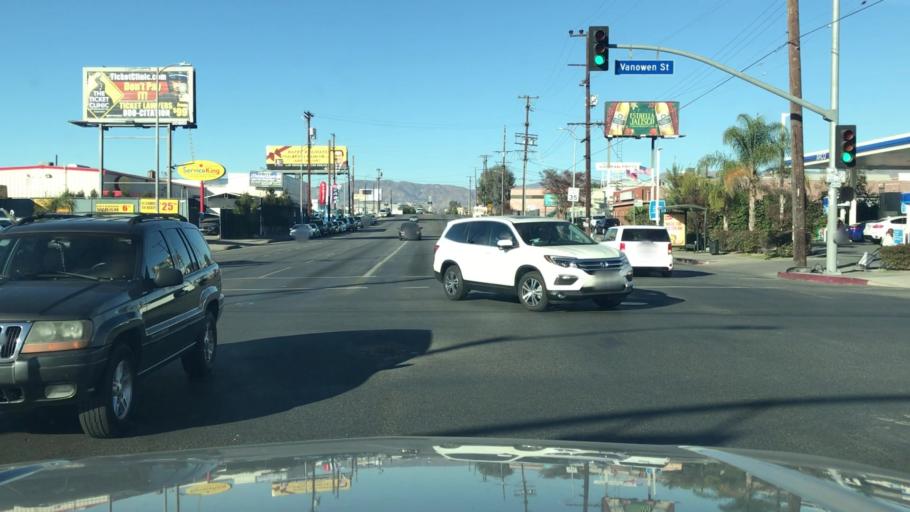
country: US
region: California
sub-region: Los Angeles County
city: North Hollywood
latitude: 34.1933
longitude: -118.3703
